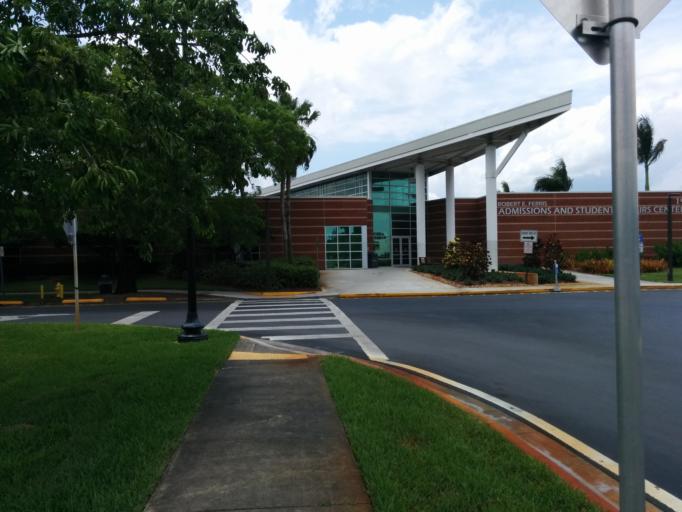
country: US
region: Florida
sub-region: Broward County
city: Davie
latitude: 26.0792
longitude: -80.2333
